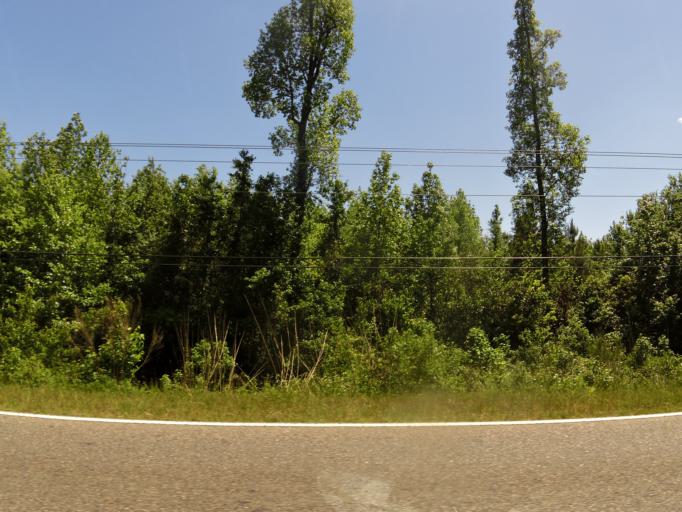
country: US
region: South Carolina
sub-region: Aiken County
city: Clearwater
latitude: 33.5094
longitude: -81.8745
